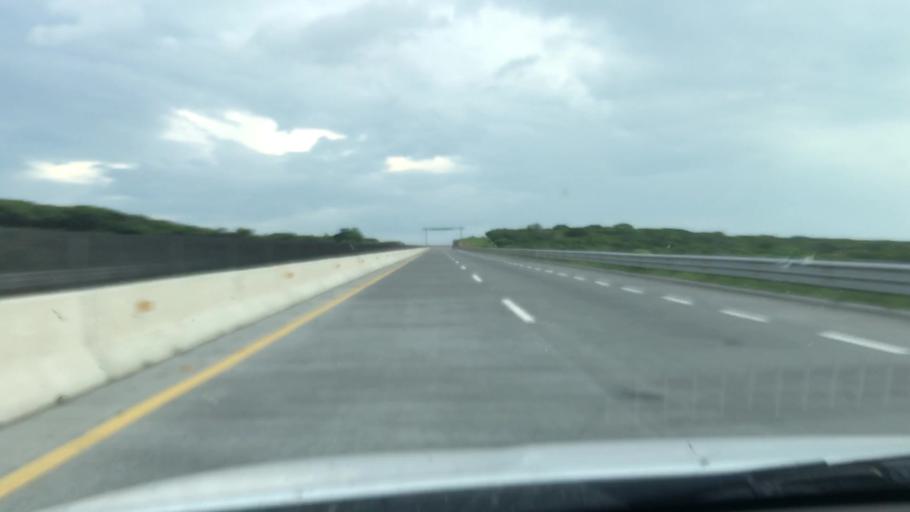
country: MX
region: Jalisco
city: Degollado
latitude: 20.3746
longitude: -102.1243
